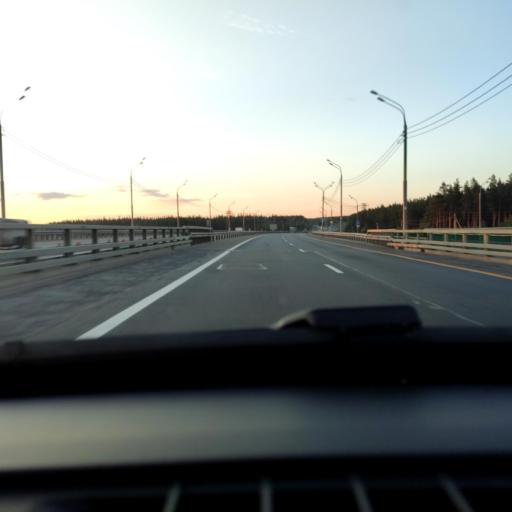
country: RU
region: Lipetsk
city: Khlevnoye
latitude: 52.2894
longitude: 39.0507
